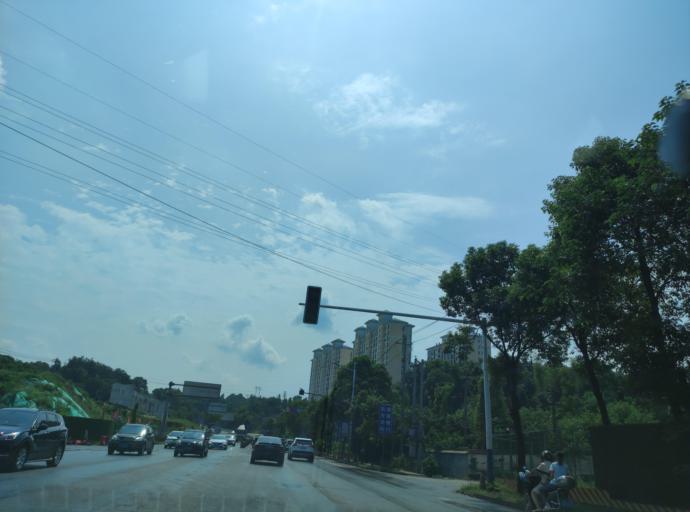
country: CN
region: Jiangxi Sheng
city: Pingxiang
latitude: 27.6524
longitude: 113.9161
